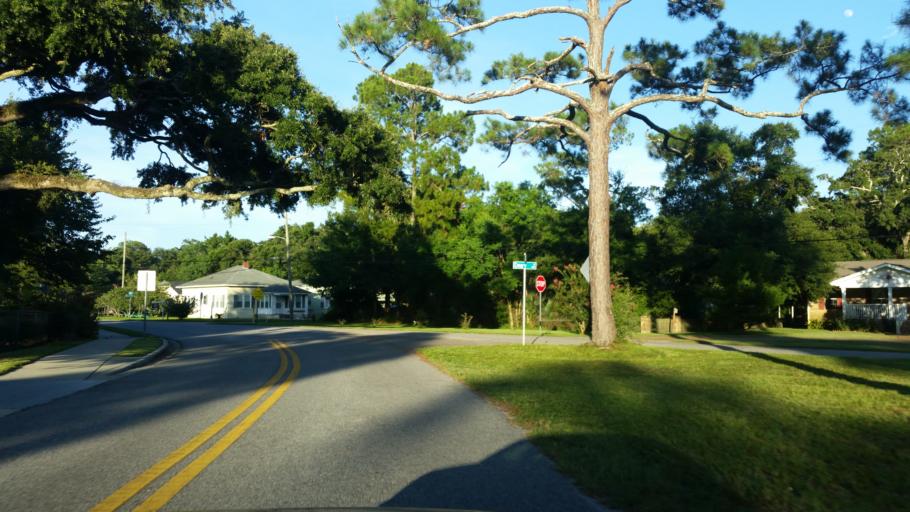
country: US
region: Florida
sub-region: Escambia County
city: Warrington
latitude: 30.3829
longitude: -87.2715
